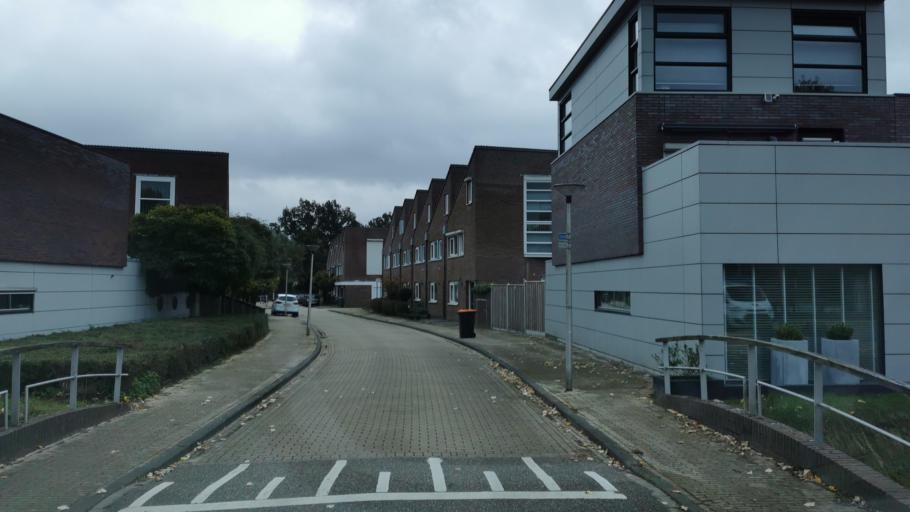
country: NL
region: Overijssel
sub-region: Gemeente Enschede
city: Enschede
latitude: 52.2121
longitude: 6.9494
